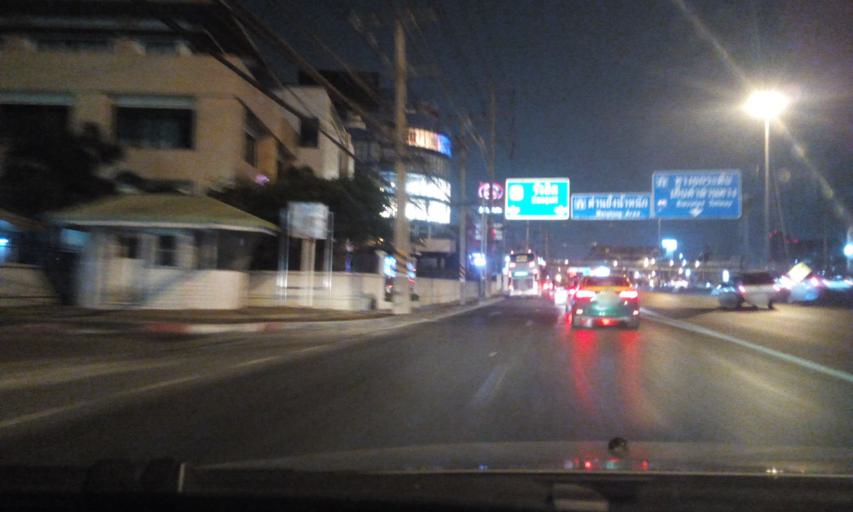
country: TH
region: Pathum Thani
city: Khlong Luang
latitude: 14.0085
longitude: 100.6154
